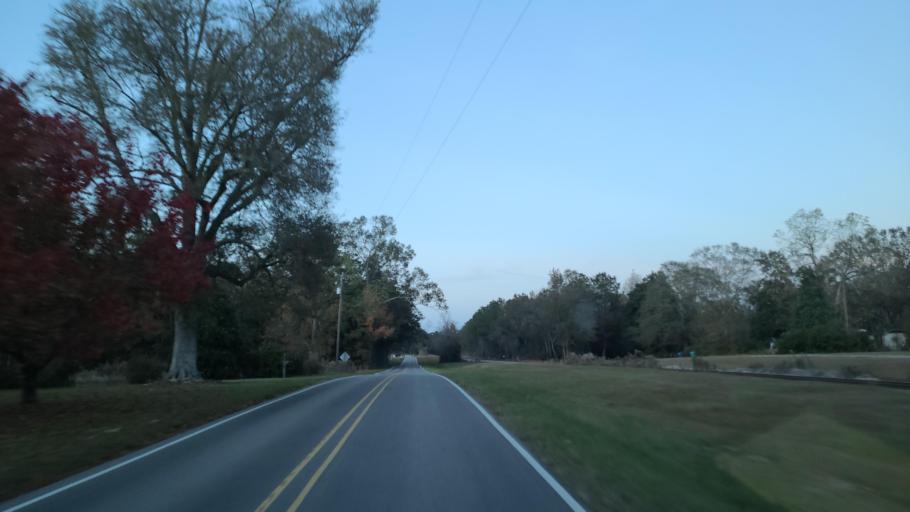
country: US
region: Mississippi
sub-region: Perry County
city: New Augusta
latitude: 31.0626
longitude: -89.1872
